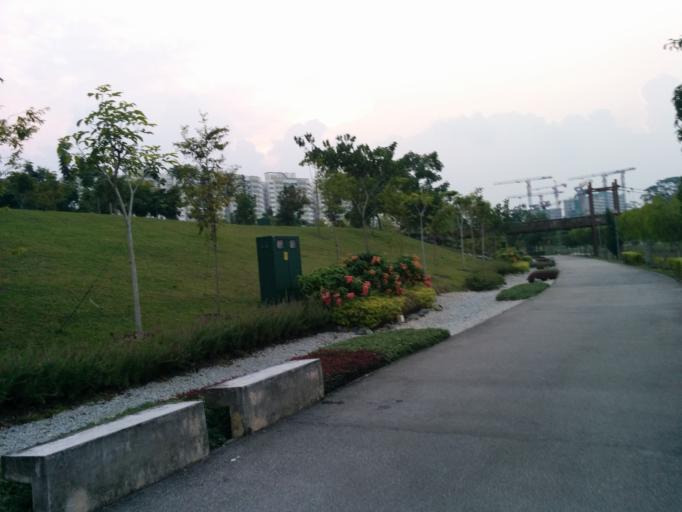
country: MY
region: Johor
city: Kampung Pasir Gudang Baru
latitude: 1.4115
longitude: 103.9048
